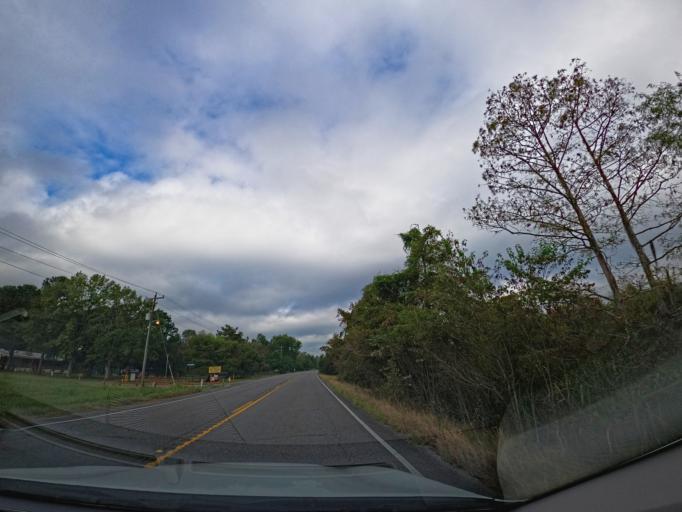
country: US
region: Louisiana
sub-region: Saint Mary Parish
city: Amelia
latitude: 29.6348
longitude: -90.9460
